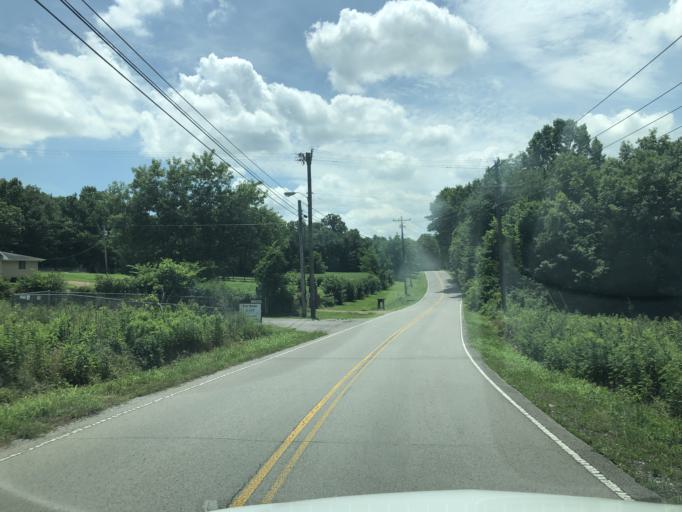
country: US
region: Tennessee
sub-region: Rutherford County
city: La Vergne
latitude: 36.0202
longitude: -86.6425
